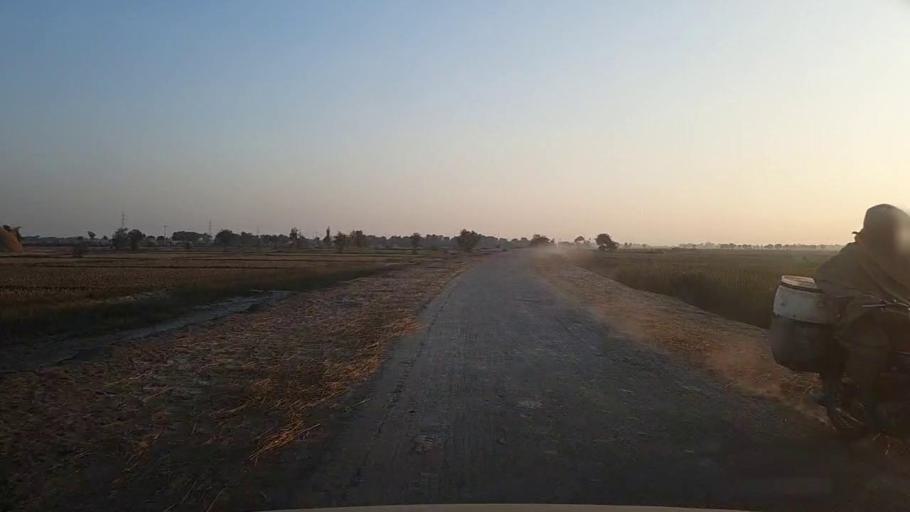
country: PK
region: Sindh
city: Khairpur Nathan Shah
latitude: 27.1764
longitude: 67.7341
